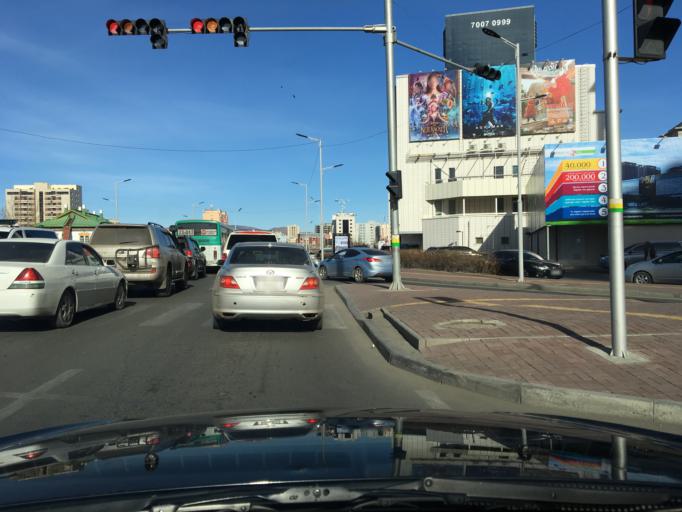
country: MN
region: Ulaanbaatar
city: Ulaanbaatar
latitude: 47.8962
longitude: 106.9085
